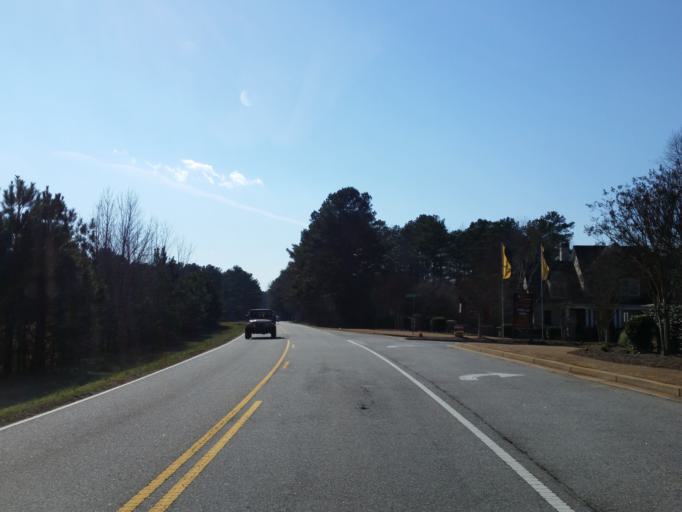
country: US
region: Georgia
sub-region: Henry County
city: Hampton
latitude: 33.4445
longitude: -84.2379
